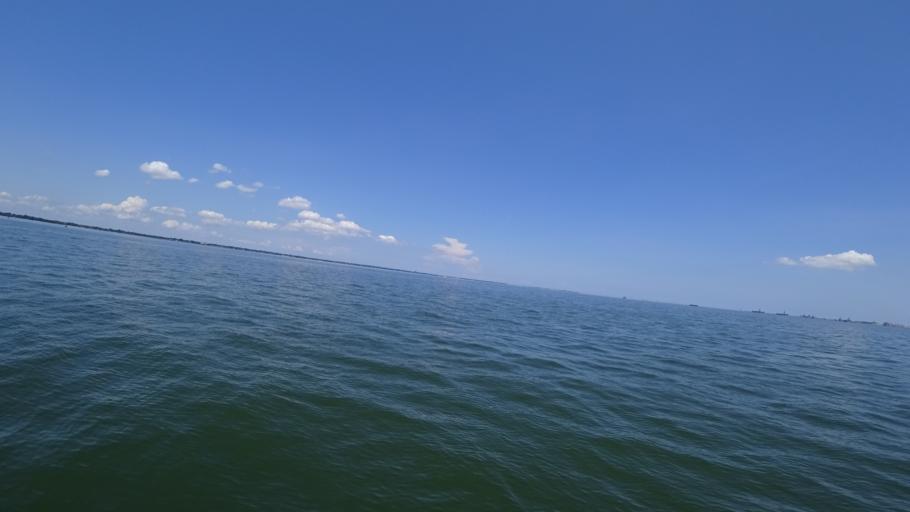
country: US
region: Virginia
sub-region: City of Newport News
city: Newport News
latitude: 36.9493
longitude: -76.3890
